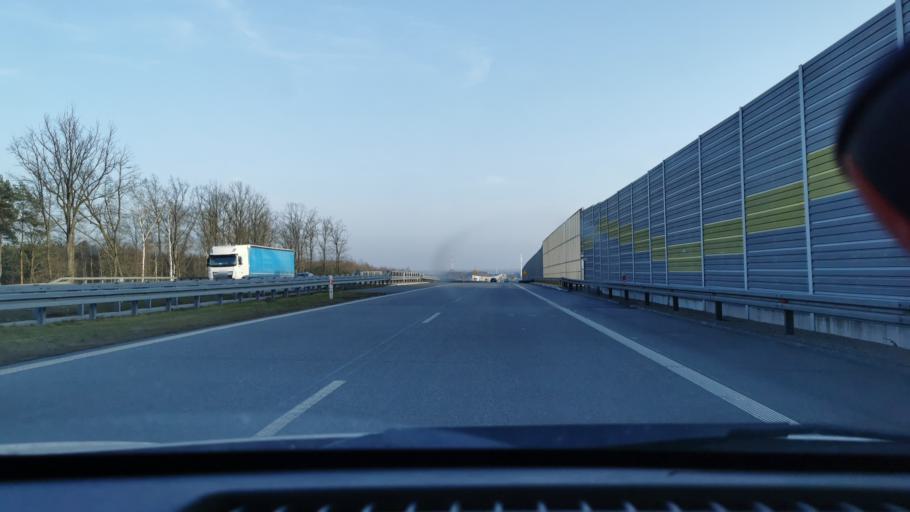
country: PL
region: Lodz Voivodeship
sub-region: Powiat zdunskowolski
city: Zdunska Wola
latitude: 51.5664
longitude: 18.9826
